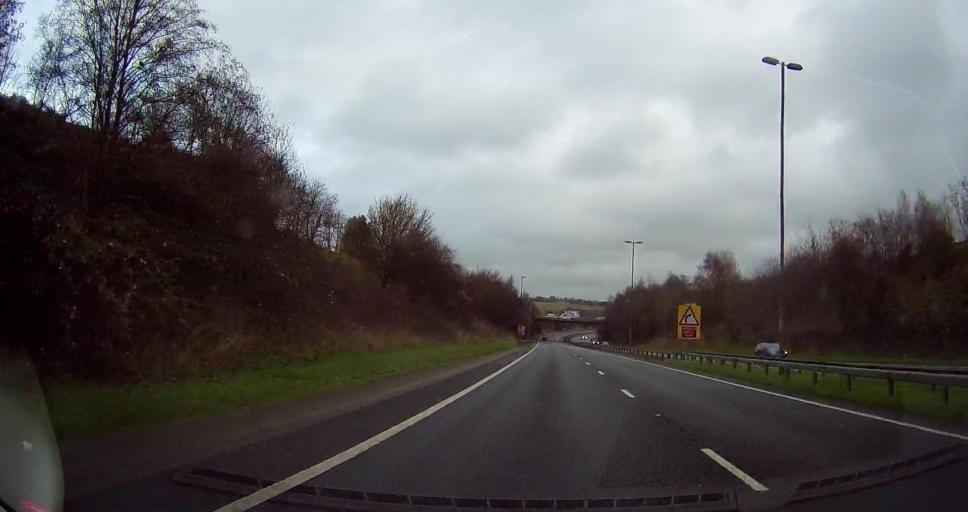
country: GB
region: England
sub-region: Kent
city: Strood
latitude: 51.4128
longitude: 0.5051
